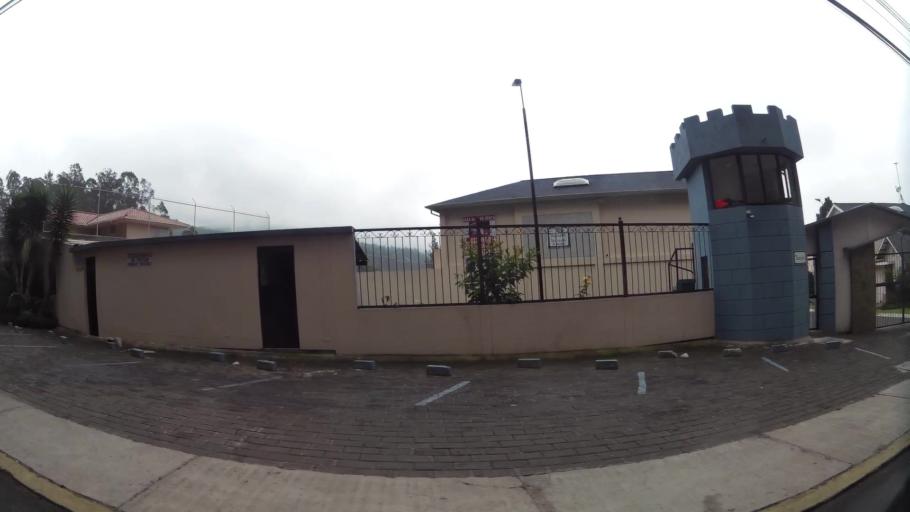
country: EC
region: Pichincha
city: Sangolqui
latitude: -0.2673
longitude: -78.4665
